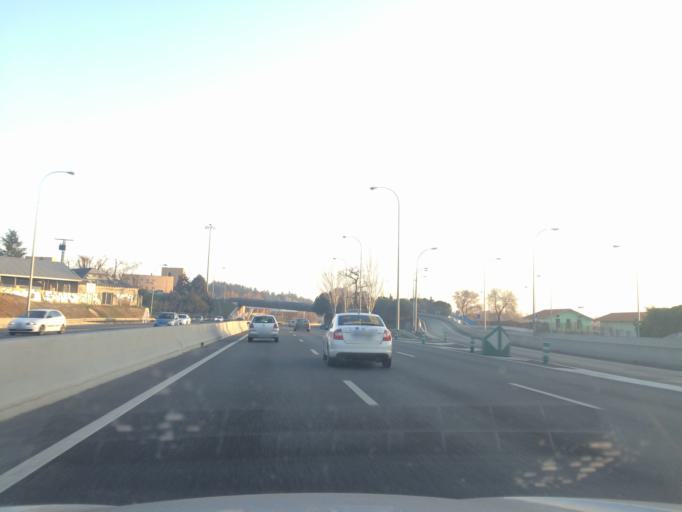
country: ES
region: Madrid
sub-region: Provincia de Madrid
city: Moncloa-Aravaca
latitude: 40.4518
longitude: -3.7430
